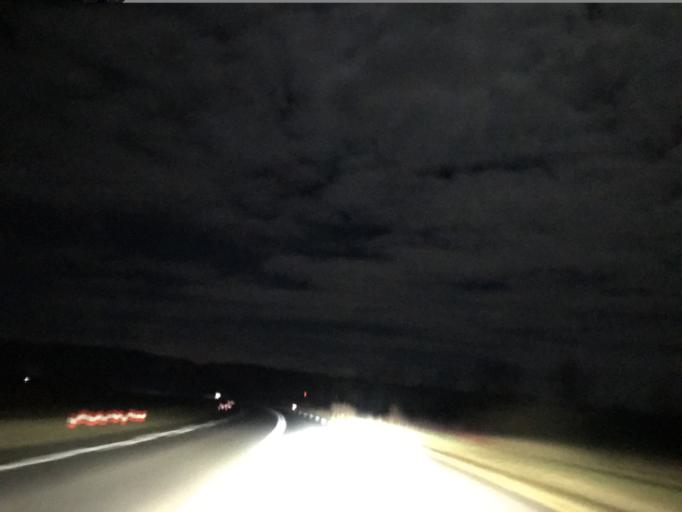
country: FR
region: Auvergne
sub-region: Departement de l'Allier
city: Saint-Yorre
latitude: 46.0417
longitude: 3.4565
